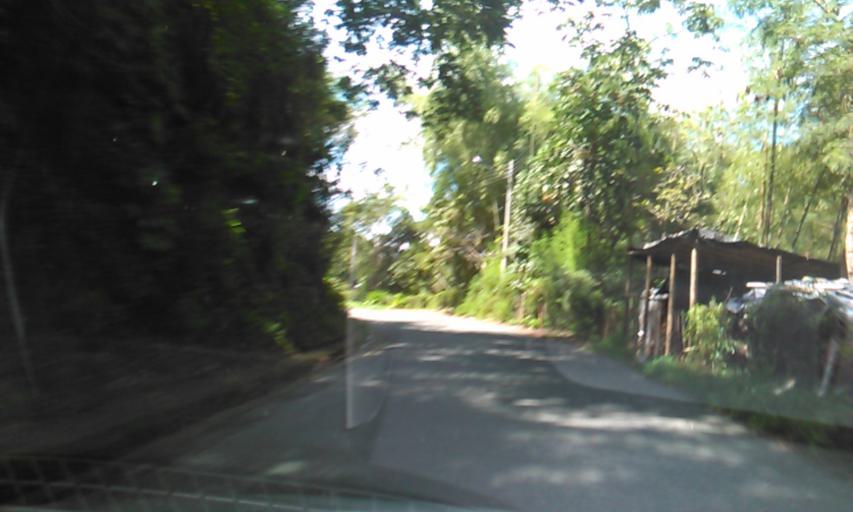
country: CO
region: Quindio
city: Cordoba
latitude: 4.4048
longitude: -75.7312
